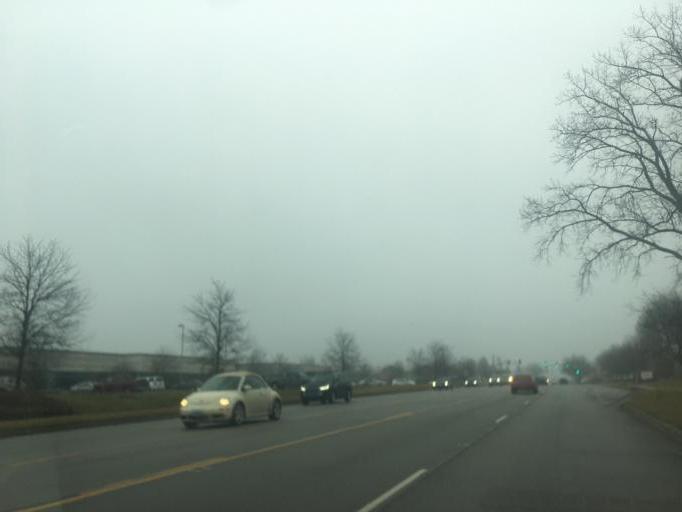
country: US
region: Illinois
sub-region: DuPage County
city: Lisle
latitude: 41.7977
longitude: -88.1011
